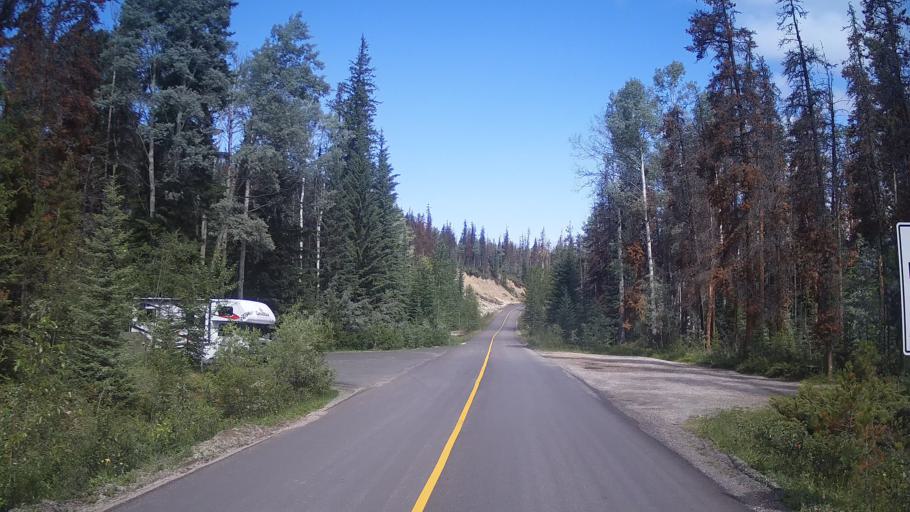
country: CA
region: Alberta
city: Jasper Park Lodge
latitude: 52.6649
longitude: -117.8886
